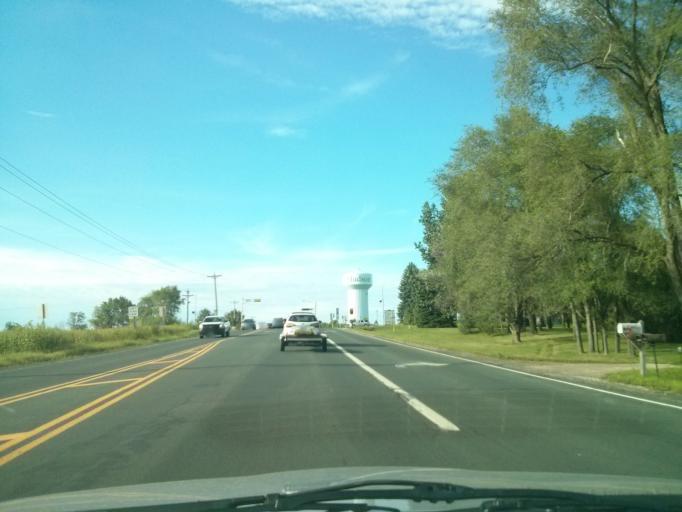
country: US
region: Wisconsin
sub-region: Saint Croix County
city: Hudson
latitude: 44.9765
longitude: -92.7211
